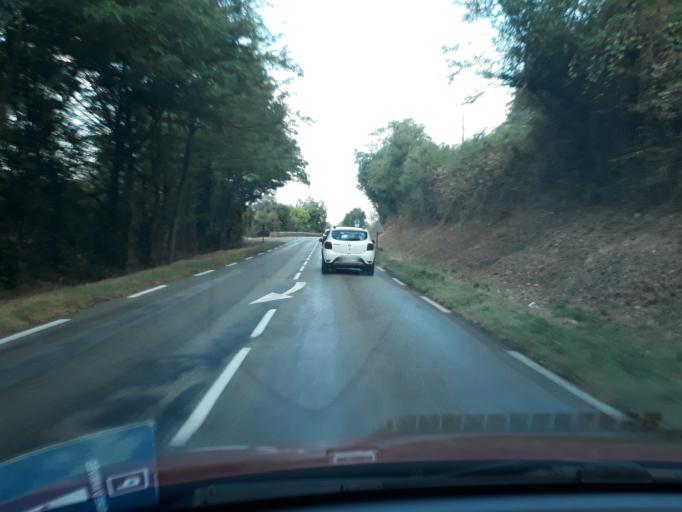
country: FR
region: Rhone-Alpes
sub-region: Departement du Rhone
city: Ampuis
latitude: 45.4769
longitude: 4.7993
